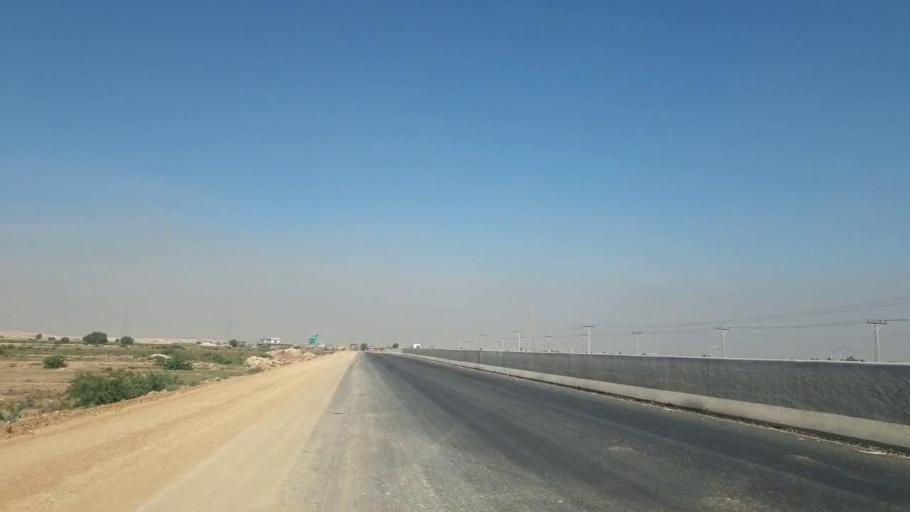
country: PK
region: Sindh
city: Jamshoro
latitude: 25.5177
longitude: 68.2740
